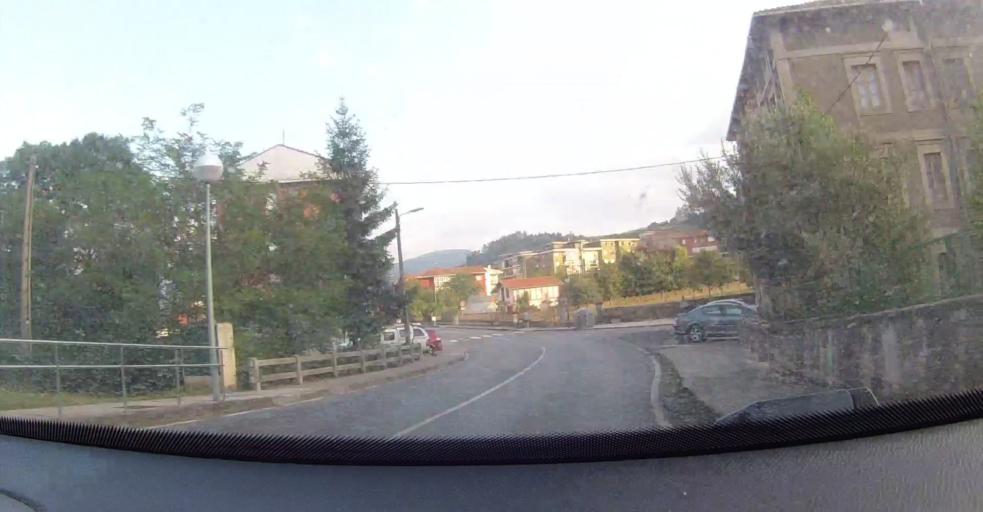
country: ES
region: Basque Country
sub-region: Bizkaia
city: Sopuerta
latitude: 43.2765
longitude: -3.1581
